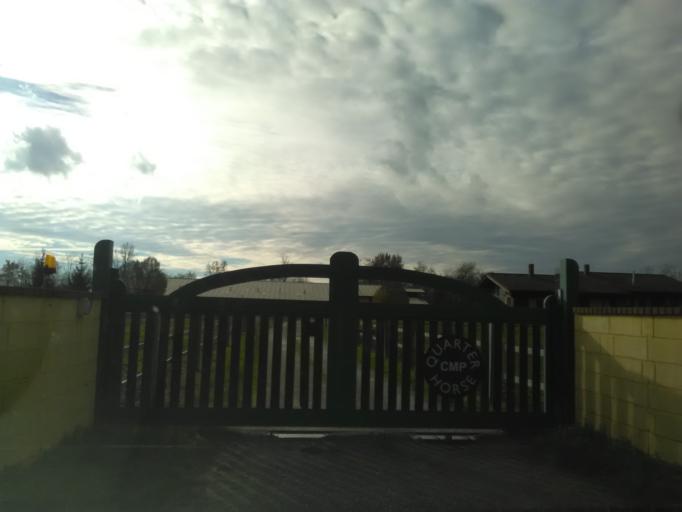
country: IT
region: Piedmont
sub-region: Provincia di Vercelli
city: Alice Castello
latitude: 45.3736
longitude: 8.0548
